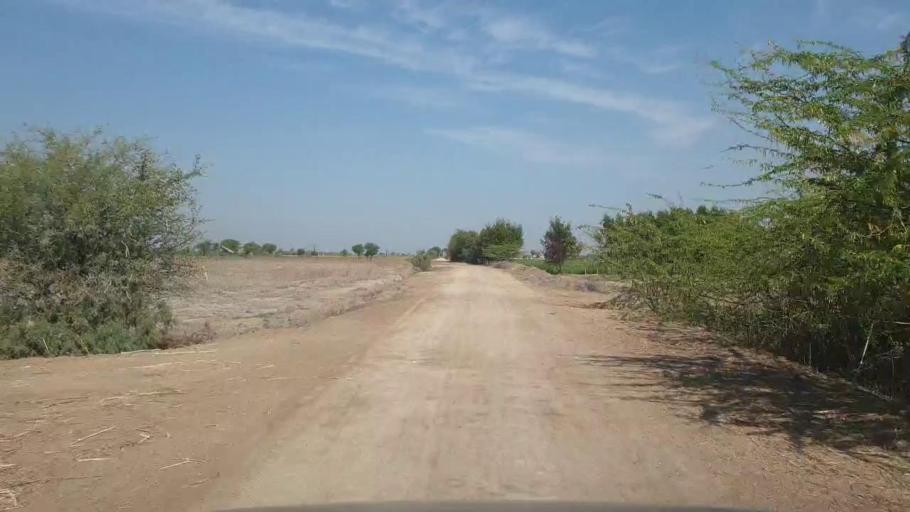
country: PK
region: Sindh
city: Mirwah Gorchani
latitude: 25.4327
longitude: 69.1861
